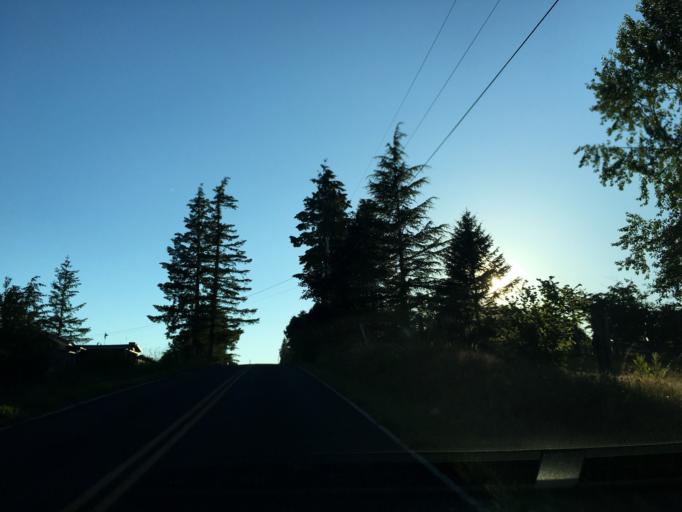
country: US
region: Washington
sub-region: Whatcom County
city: Geneva
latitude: 48.8150
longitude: -122.4047
